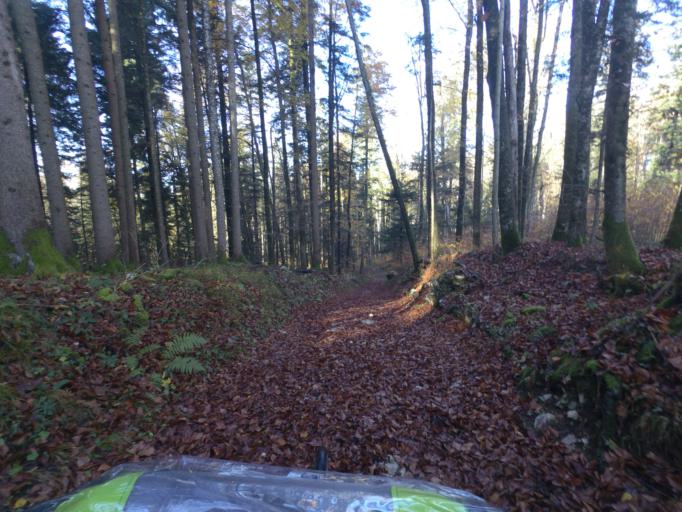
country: AT
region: Salzburg
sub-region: Politischer Bezirk Hallein
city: Adnet
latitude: 47.6819
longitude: 13.1529
